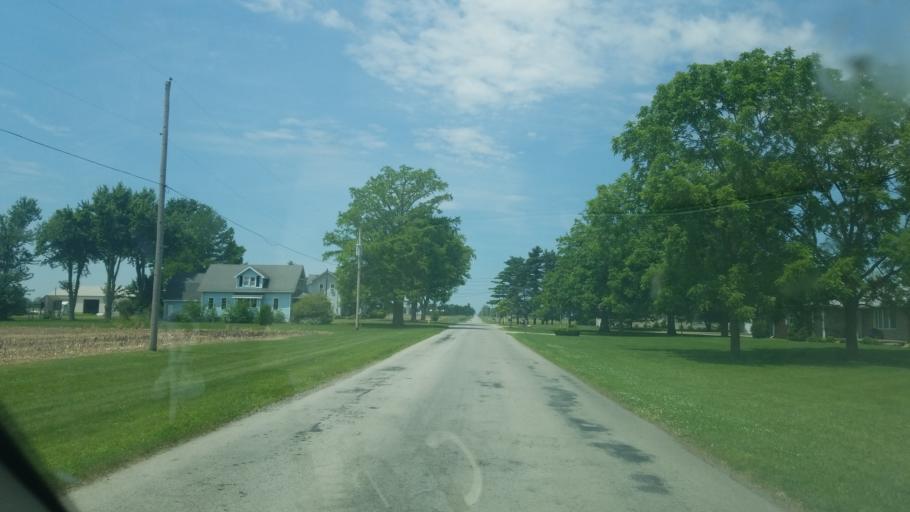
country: US
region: Ohio
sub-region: Wood County
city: North Baltimore
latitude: 41.2538
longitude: -83.6123
